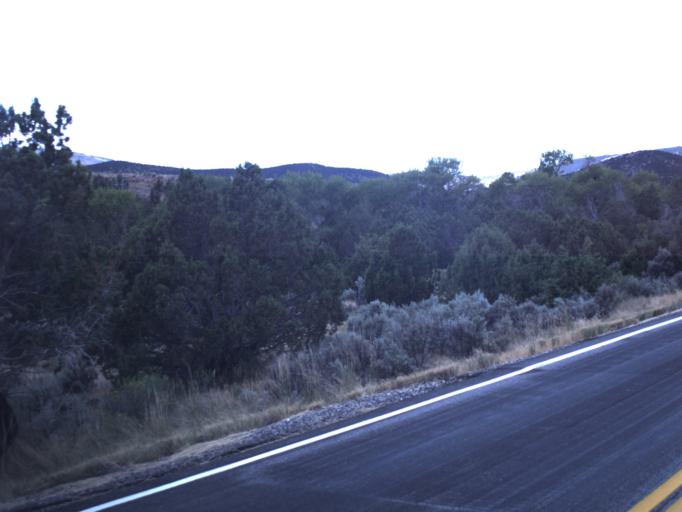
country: US
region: Utah
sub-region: Tooele County
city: Grantsville
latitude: 40.3326
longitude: -112.5181
